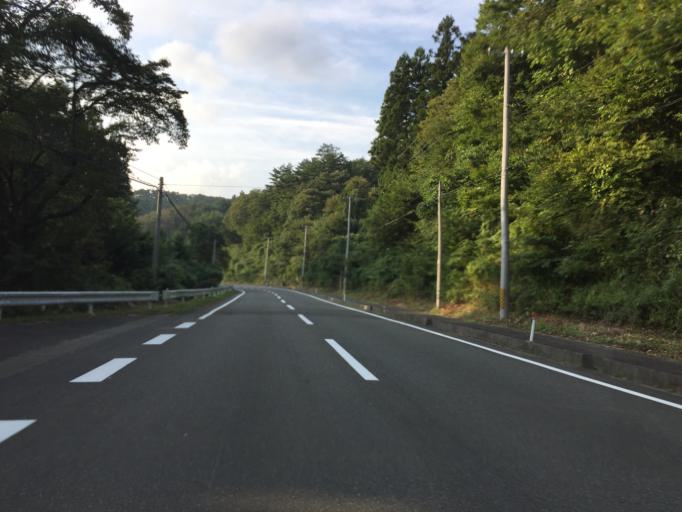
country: JP
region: Fukushima
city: Namie
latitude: 37.5507
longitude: 140.8413
